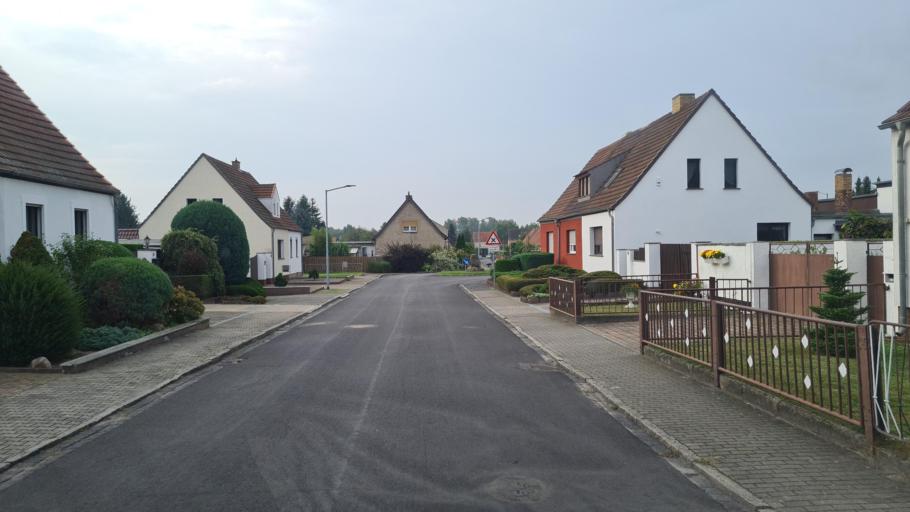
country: DE
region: Brandenburg
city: Lauchhammer
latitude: 51.4949
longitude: 13.7725
